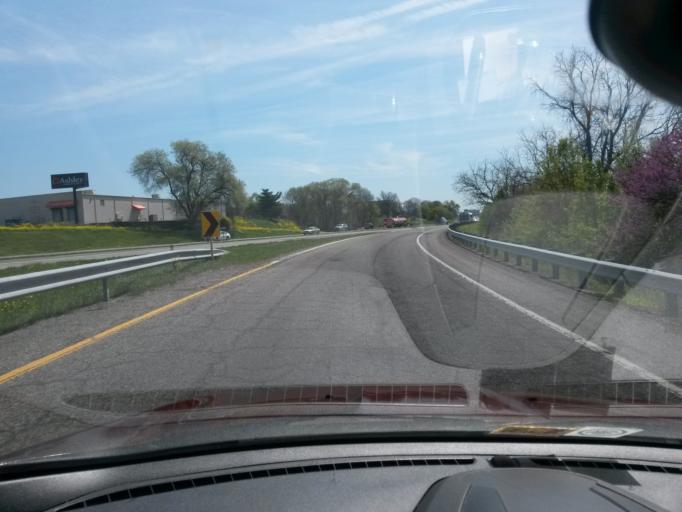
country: US
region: Virginia
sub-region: Roanoke County
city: Hollins
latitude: 37.3068
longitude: -79.9723
